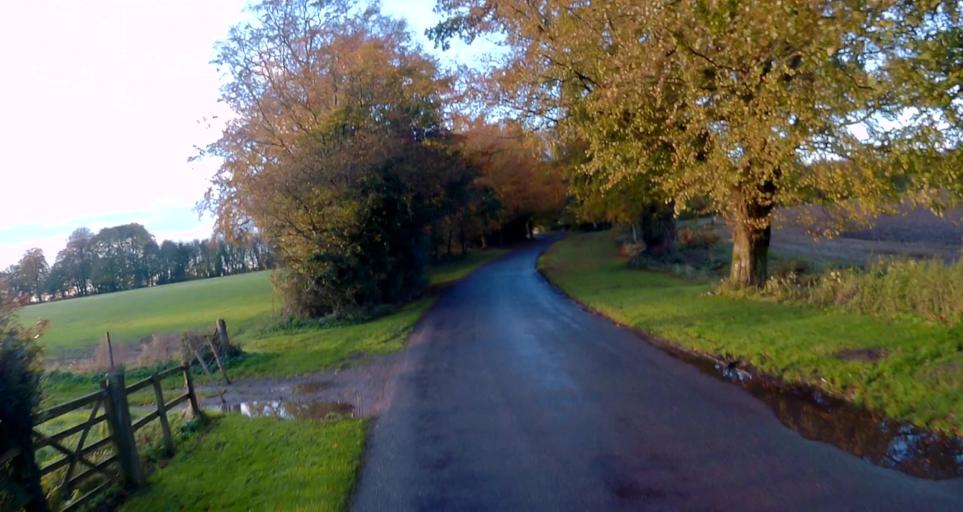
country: GB
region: England
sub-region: Hampshire
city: Basingstoke
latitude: 51.2180
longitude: -1.1154
